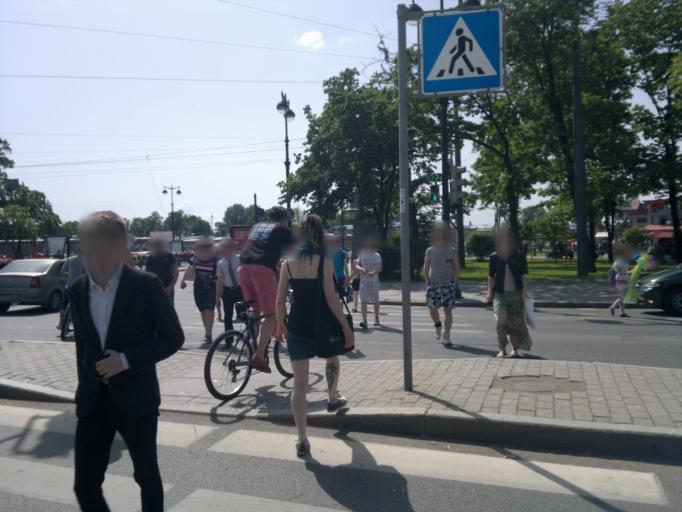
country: RU
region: St.-Petersburg
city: Petrogradka
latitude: 59.9534
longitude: 30.3236
